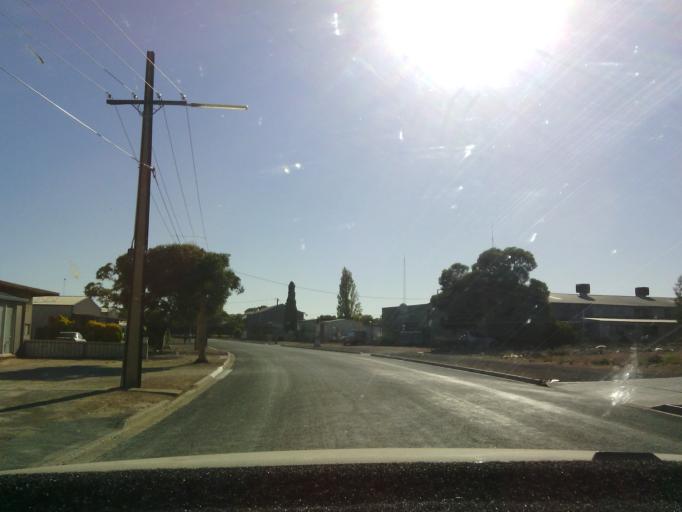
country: AU
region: South Australia
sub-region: Berri and Barmera
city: Berri
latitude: -34.2713
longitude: 140.6023
